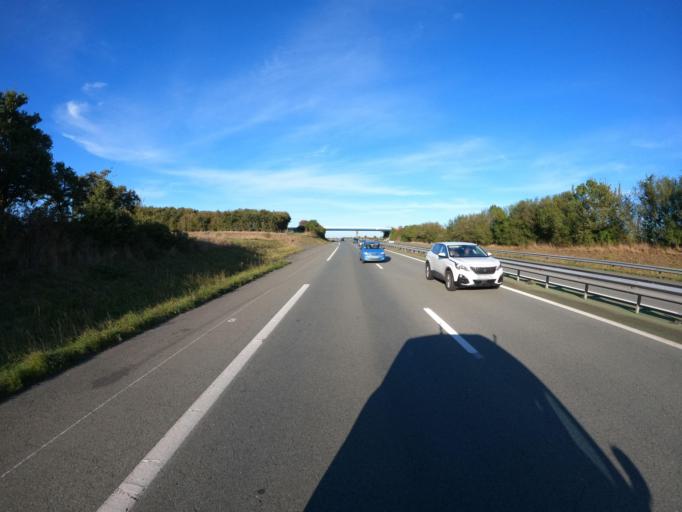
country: FR
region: Pays de la Loire
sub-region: Departement de Maine-et-Loire
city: Trementines
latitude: 47.1770
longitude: -0.7885
